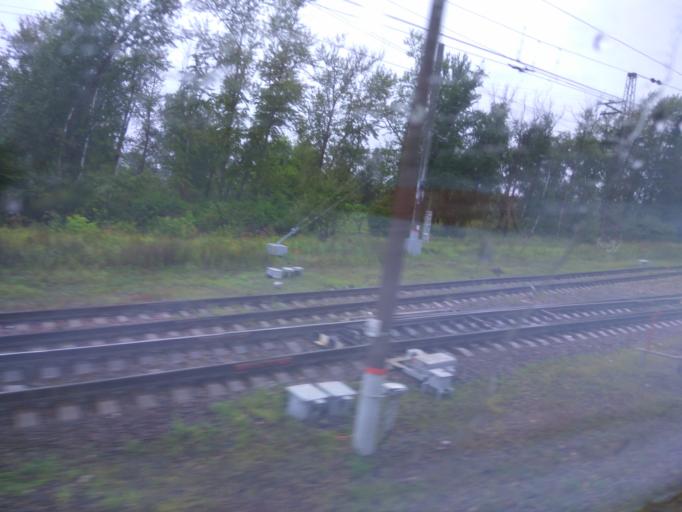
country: RU
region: Moskovskaya
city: Zhilevo
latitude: 54.9839
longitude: 38.0325
